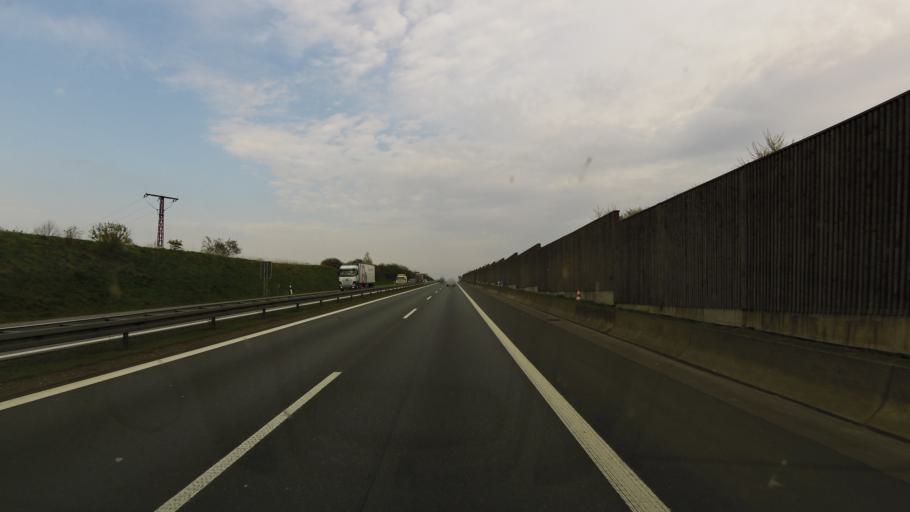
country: DE
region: Saxony
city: Bosenbrunn
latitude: 50.4334
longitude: 12.1099
